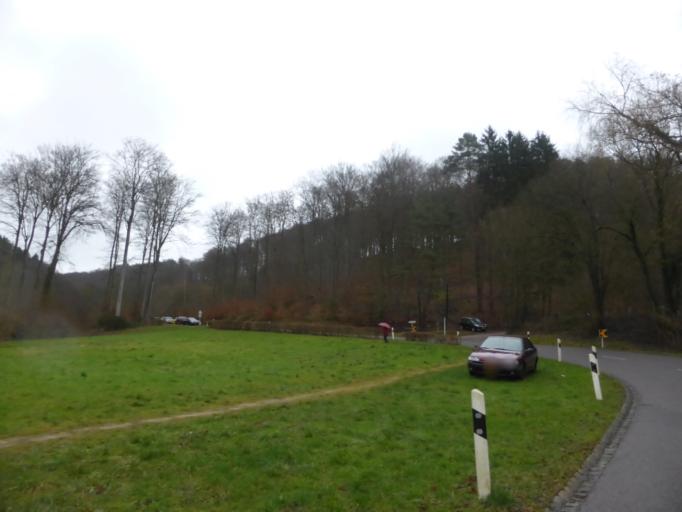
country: LU
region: Luxembourg
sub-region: Canton de Mersch
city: Lintgen
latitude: 49.7193
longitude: 6.1488
